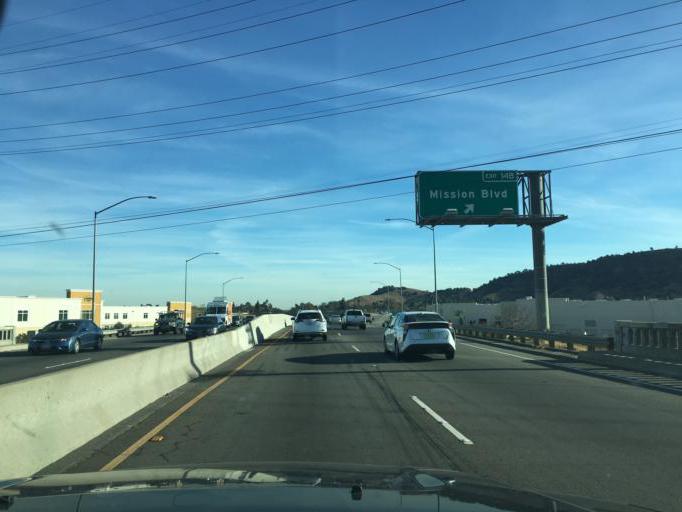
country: US
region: California
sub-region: Los Angeles County
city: Pomona
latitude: 34.0569
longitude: -117.7847
